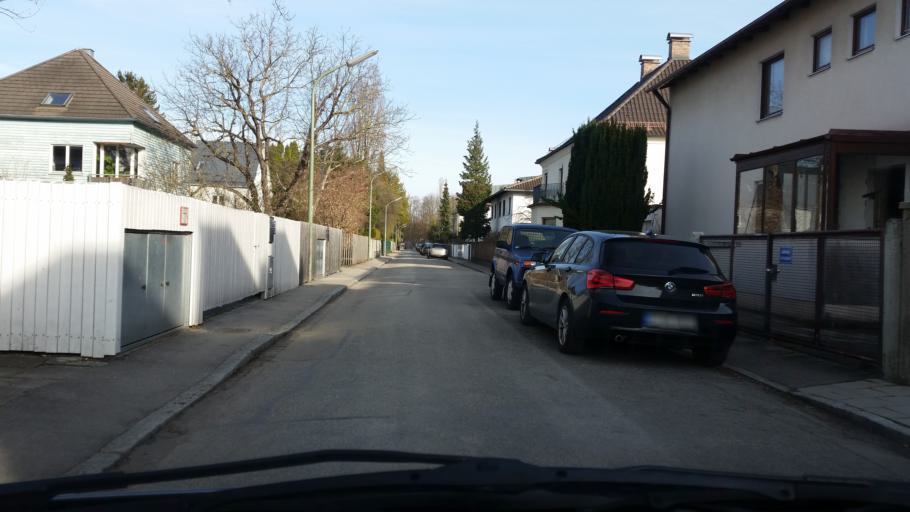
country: DE
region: Bavaria
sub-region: Upper Bavaria
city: Munich
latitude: 48.1261
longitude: 11.5180
